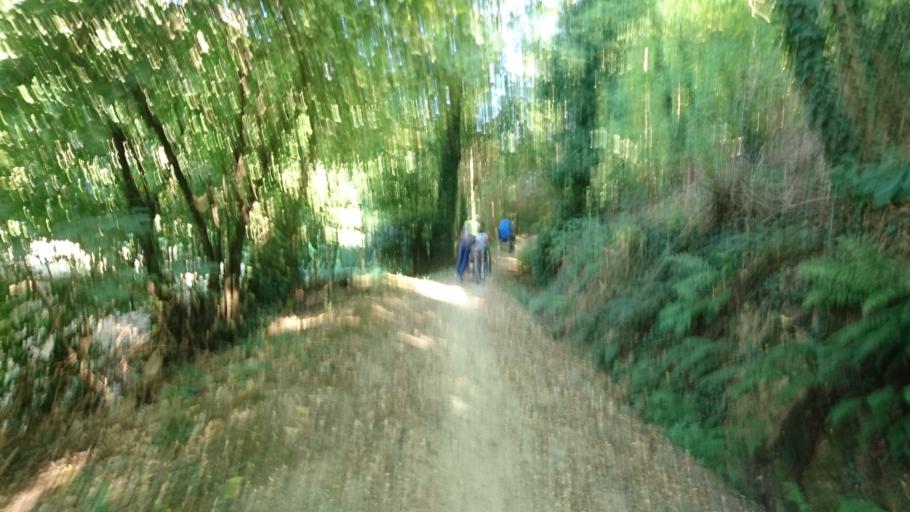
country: IT
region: Veneto
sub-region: Provincia di Padova
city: Galzignano
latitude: 45.3132
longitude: 11.7484
